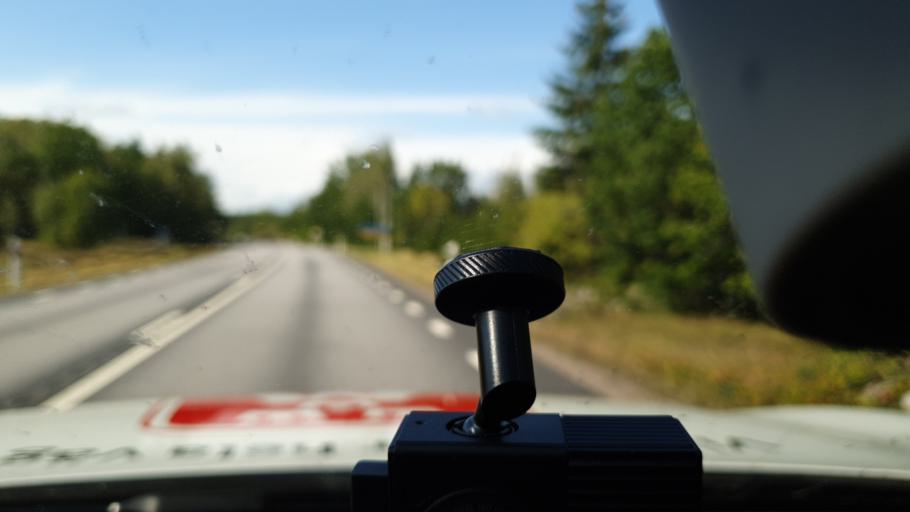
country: SE
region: Kalmar
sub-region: Vasterviks Kommun
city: Ankarsrum
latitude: 57.7060
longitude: 16.1505
